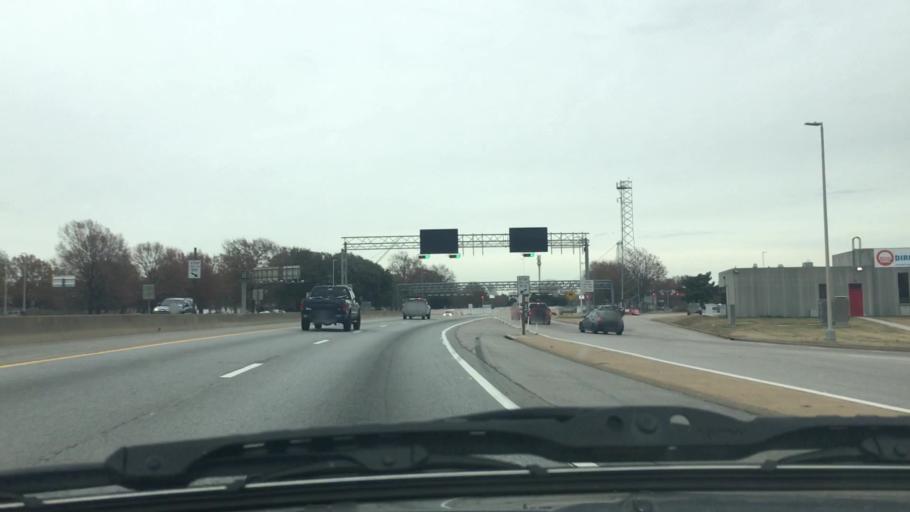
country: US
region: Virginia
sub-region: City of Portsmouth
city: Portsmouth
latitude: 36.8307
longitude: -76.3047
